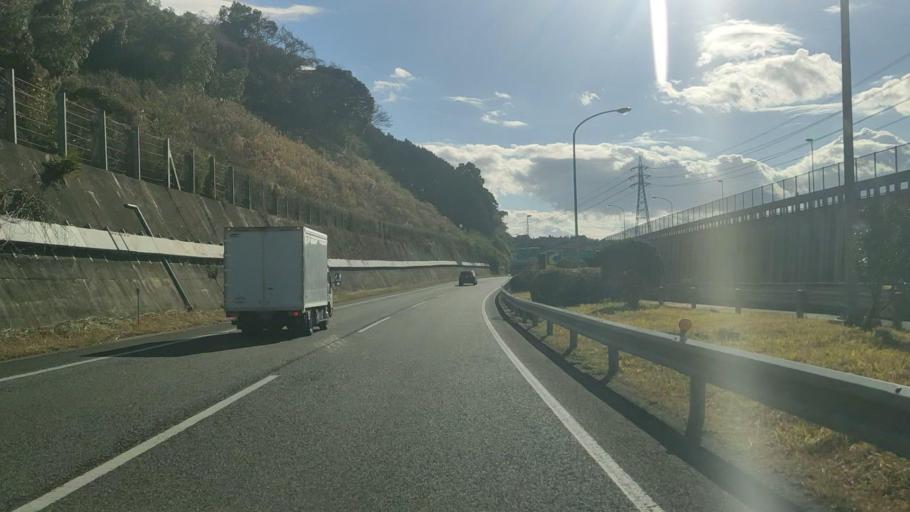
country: JP
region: Fukuoka
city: Kitakyushu
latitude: 33.8455
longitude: 130.7665
